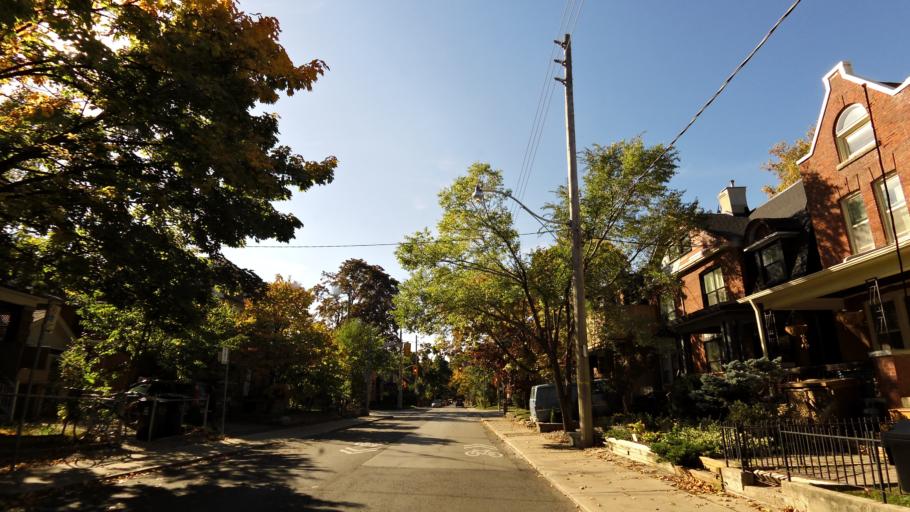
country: CA
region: Ontario
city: Toronto
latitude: 43.6563
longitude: -79.4267
